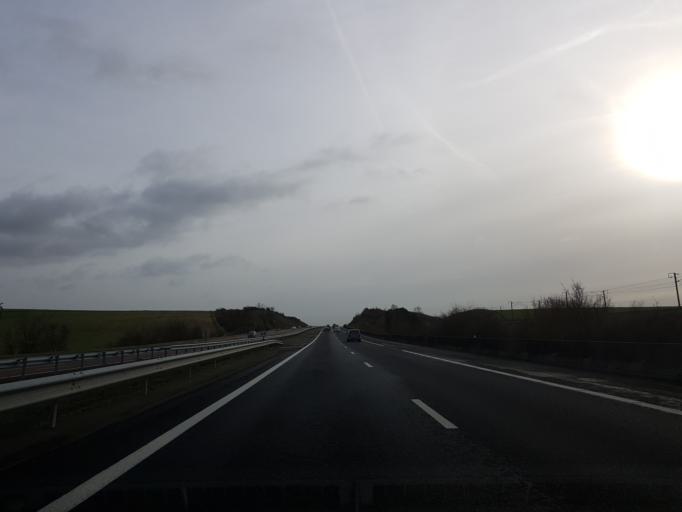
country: FR
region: Bourgogne
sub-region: Departement de l'Yonne
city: Courlon-sur-Yonne
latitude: 48.3363
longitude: 3.2060
